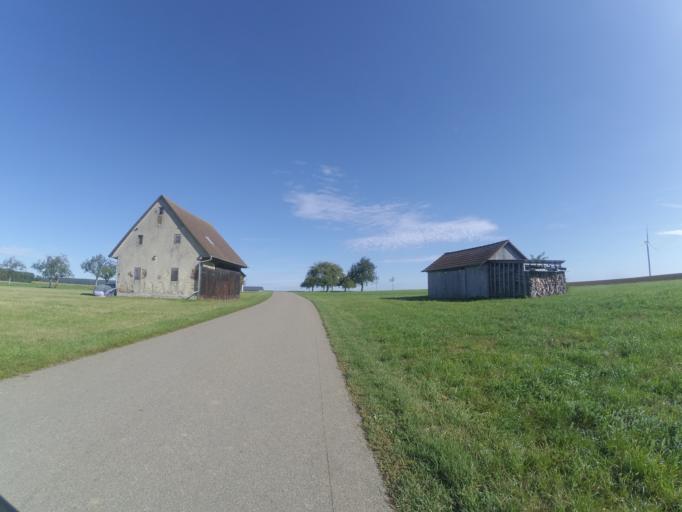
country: DE
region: Baden-Wuerttemberg
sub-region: Tuebingen Region
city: Holzkirch
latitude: 48.5349
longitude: 9.9955
